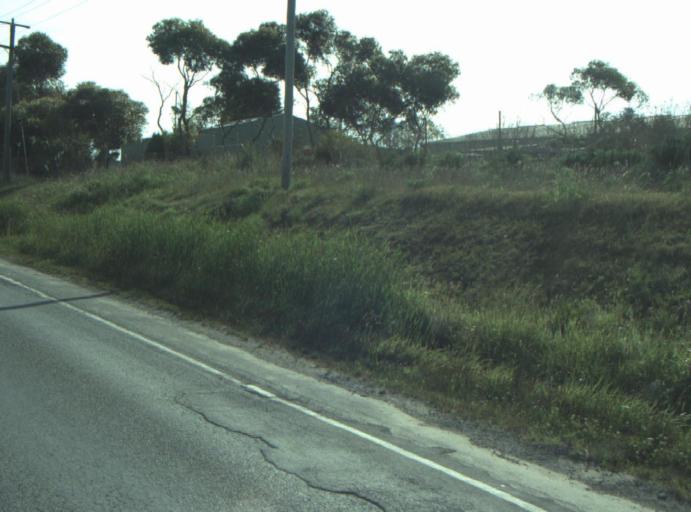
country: AU
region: Victoria
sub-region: Greater Geelong
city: Leopold
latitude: -38.1635
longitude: 144.4267
